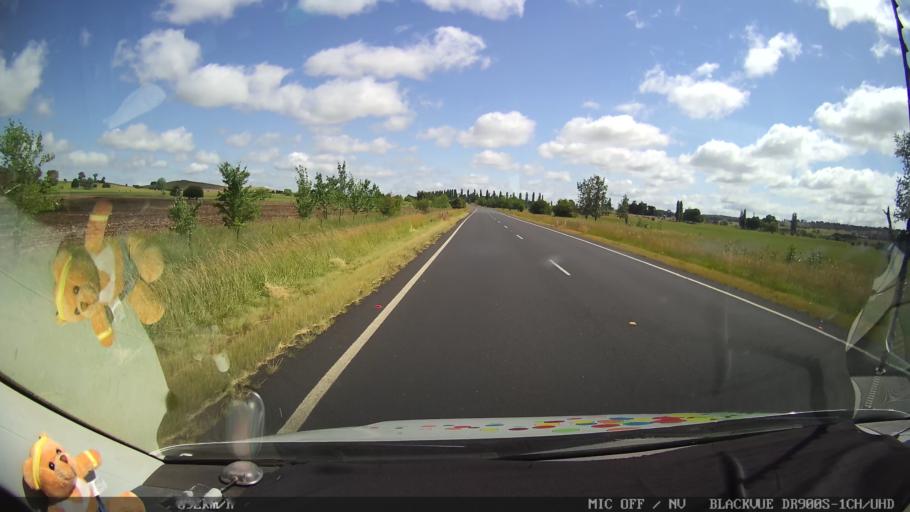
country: AU
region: New South Wales
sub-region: Glen Innes Severn
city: Glen Innes
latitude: -29.8510
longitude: 151.7374
